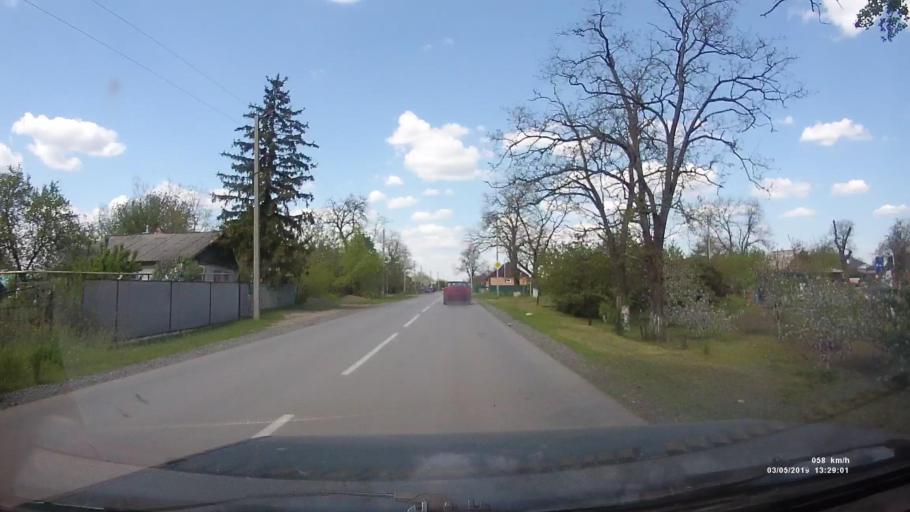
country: RU
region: Rostov
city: Semikarakorsk
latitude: 47.5804
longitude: 40.8417
